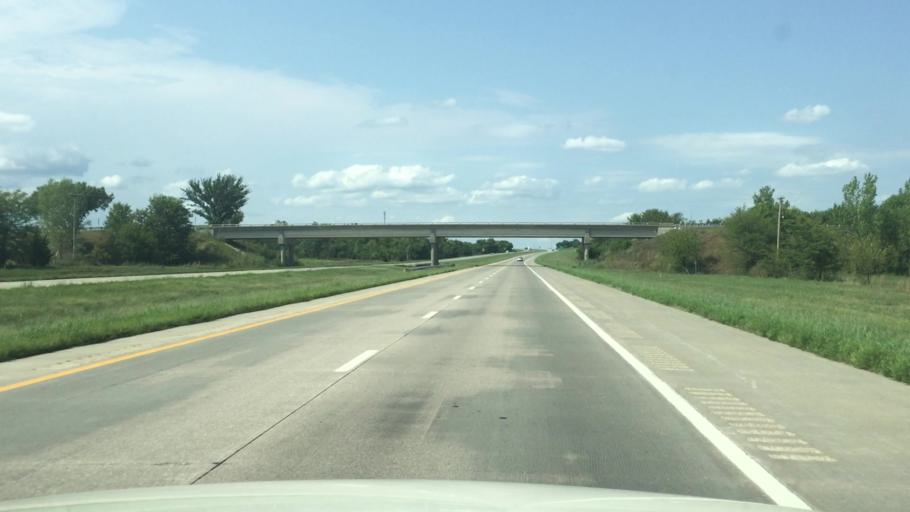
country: US
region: Kansas
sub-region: Linn County
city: La Cygne
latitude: 38.4603
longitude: -94.6863
